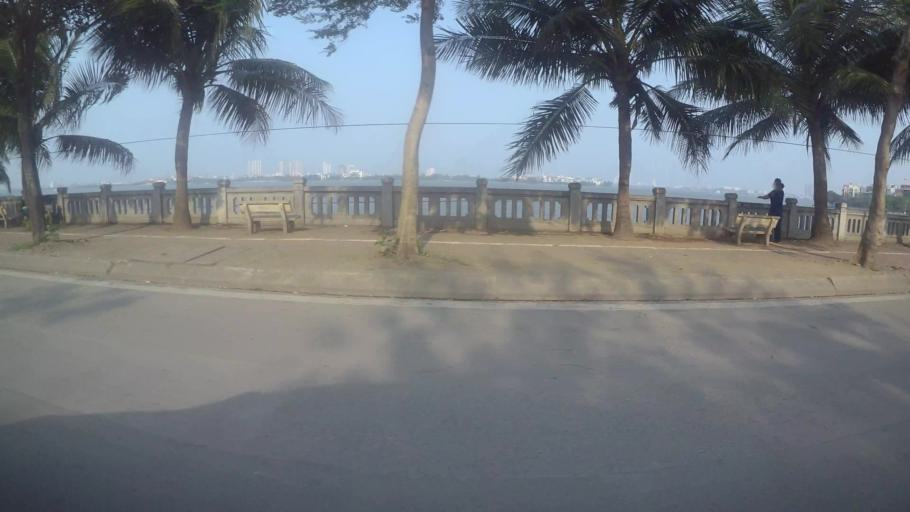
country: VN
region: Ha Noi
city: Tay Ho
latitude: 21.0582
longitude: 105.8089
